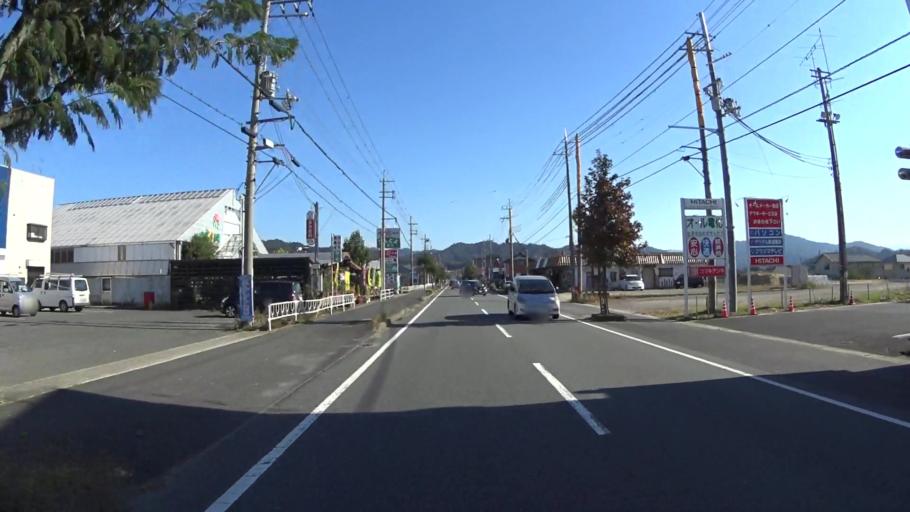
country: JP
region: Kyoto
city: Miyazu
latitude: 35.5905
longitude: 135.0941
